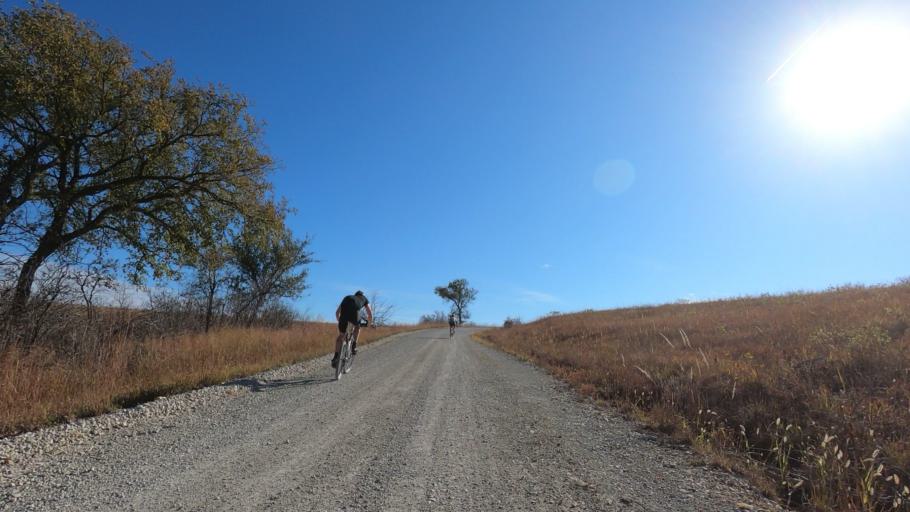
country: US
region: Kansas
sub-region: Pottawatomie County
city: Westmoreland
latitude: 39.4798
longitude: -96.5882
